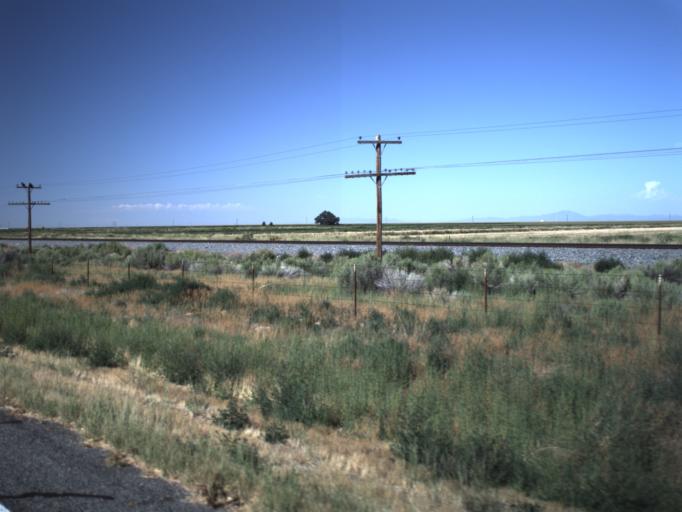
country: US
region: Utah
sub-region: Millard County
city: Delta
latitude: 39.5498
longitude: -112.3570
